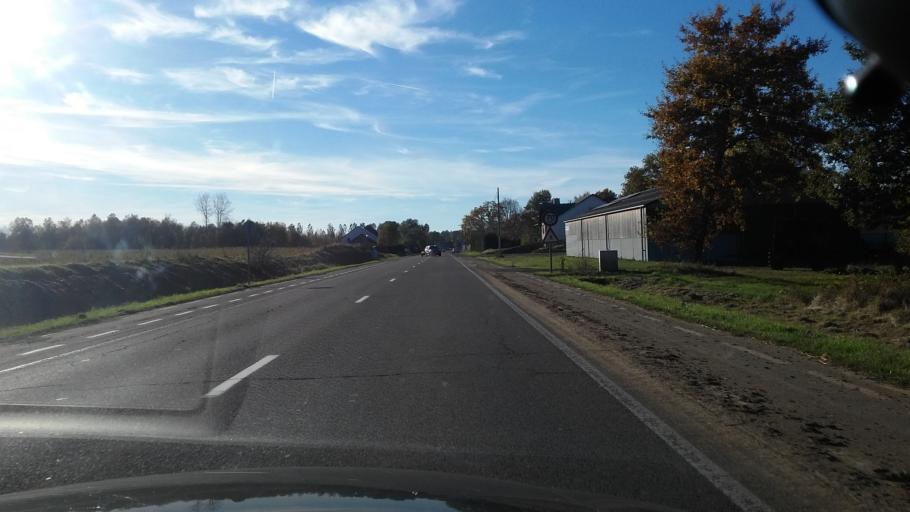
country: BE
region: Wallonia
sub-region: Province du Luxembourg
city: Saint-Leger
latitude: 49.6701
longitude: 5.6786
